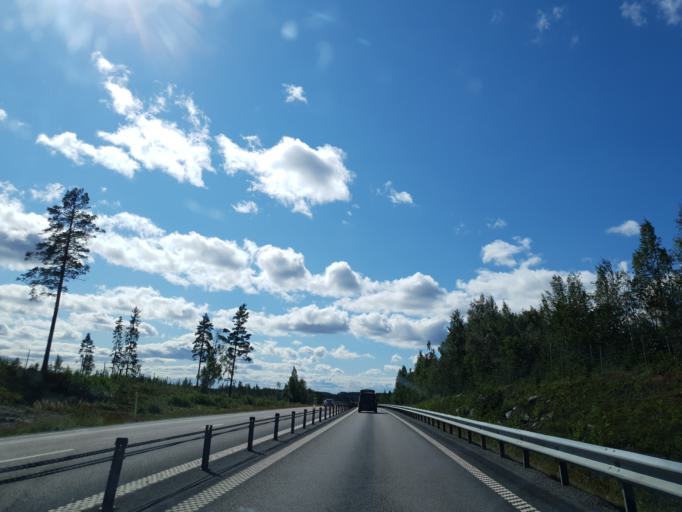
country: SE
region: Vaesternorrland
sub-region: OErnskoeldsviks Kommun
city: Husum
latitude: 63.4493
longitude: 19.2253
